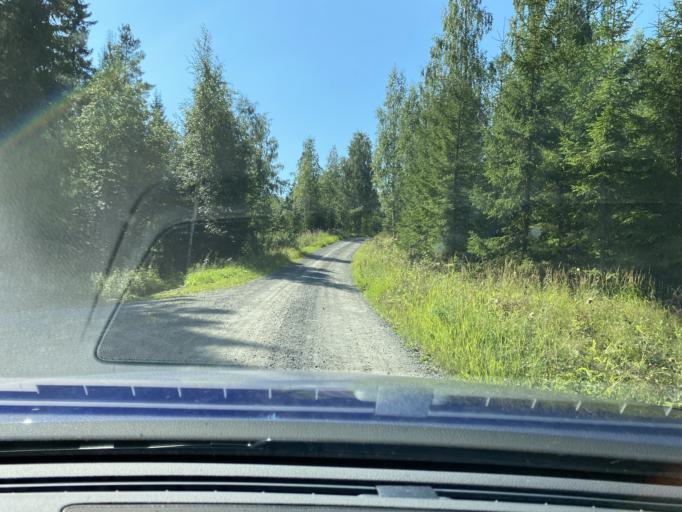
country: FI
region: Central Finland
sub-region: Jaemsae
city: Jaemsae
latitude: 61.8502
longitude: 25.3818
